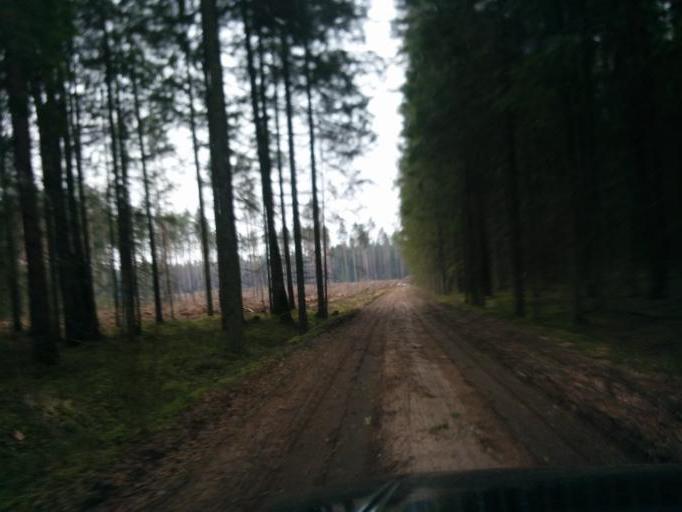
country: LV
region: Ikskile
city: Ikskile
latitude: 56.8062
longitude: 24.4828
